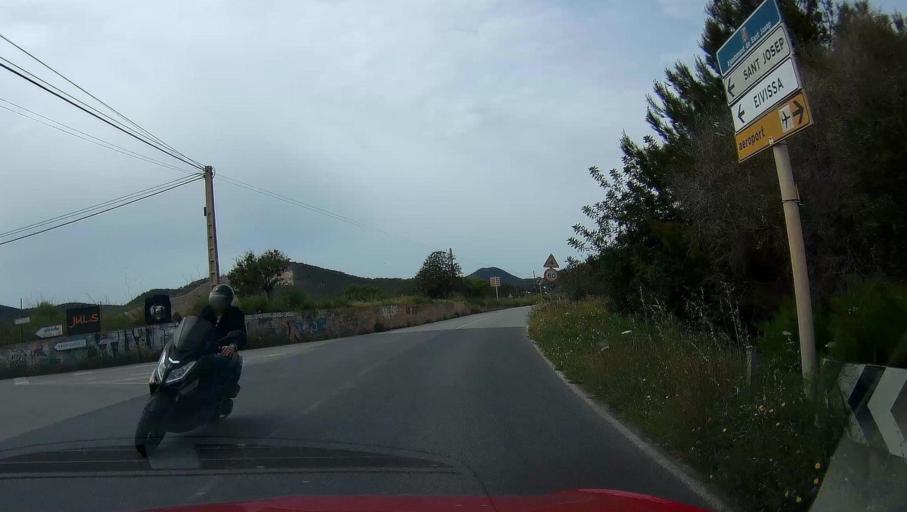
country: ES
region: Balearic Islands
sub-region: Illes Balears
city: Ibiza
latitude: 38.8801
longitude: 1.3615
